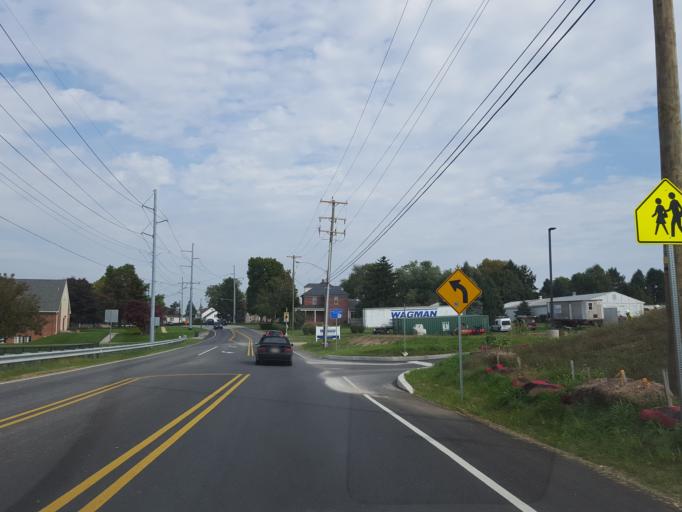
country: US
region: Pennsylvania
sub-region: York County
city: Valley View
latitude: 39.9451
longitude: -76.6925
